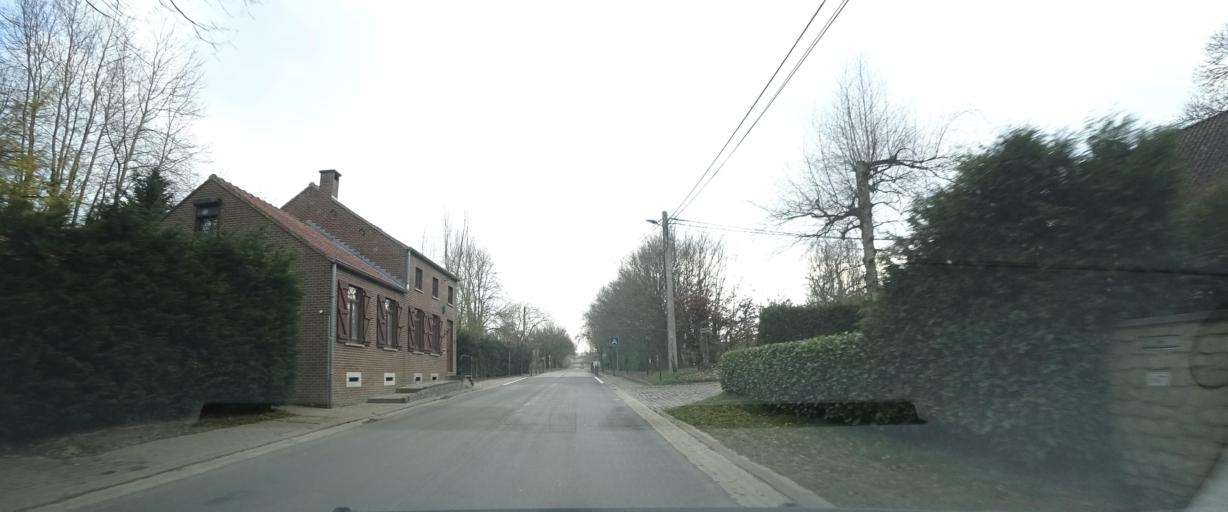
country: BE
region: Wallonia
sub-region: Province du Brabant Wallon
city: Chaumont-Gistoux
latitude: 50.6728
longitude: 4.6834
